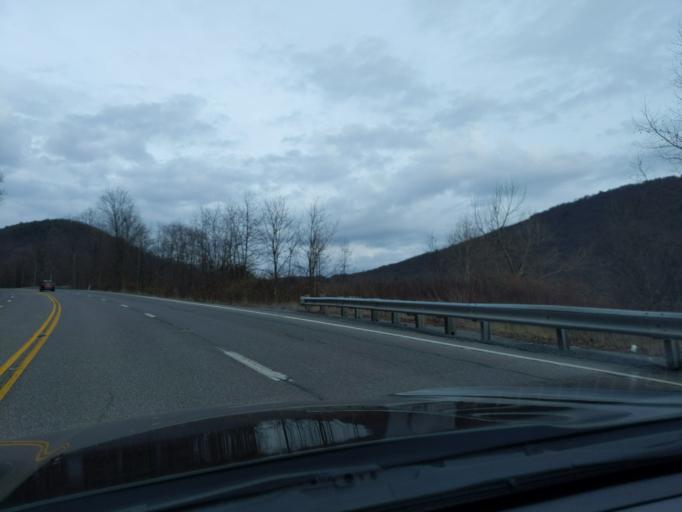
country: US
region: Pennsylvania
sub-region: Blair County
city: Williamsburg
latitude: 40.4881
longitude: -78.2460
